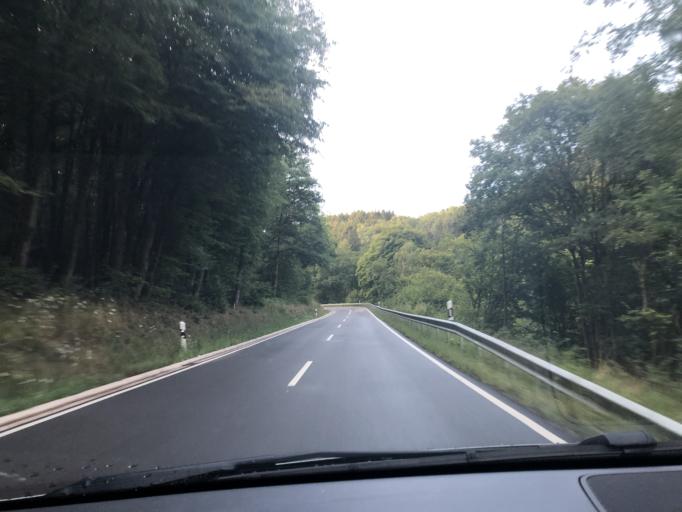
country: DE
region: Rheinland-Pfalz
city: Grimburg
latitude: 49.6121
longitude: 6.8836
